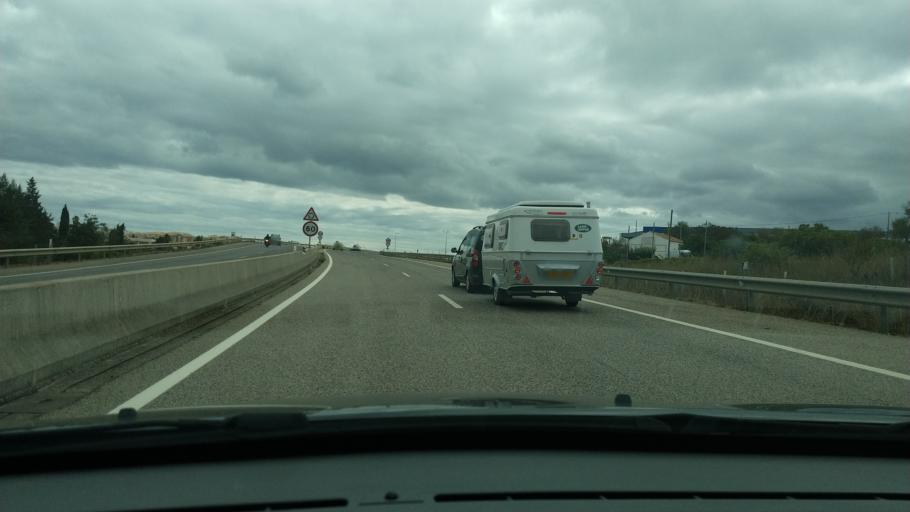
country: PT
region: Faro
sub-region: Lagos
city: Lagos
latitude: 37.1044
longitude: -8.6960
